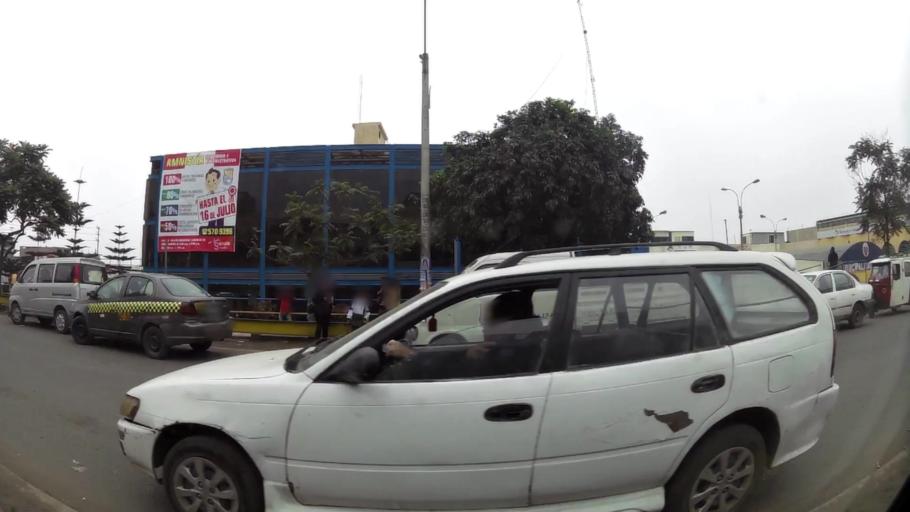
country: PE
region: Lima
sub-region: Lima
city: Surco
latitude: -12.2130
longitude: -76.9370
